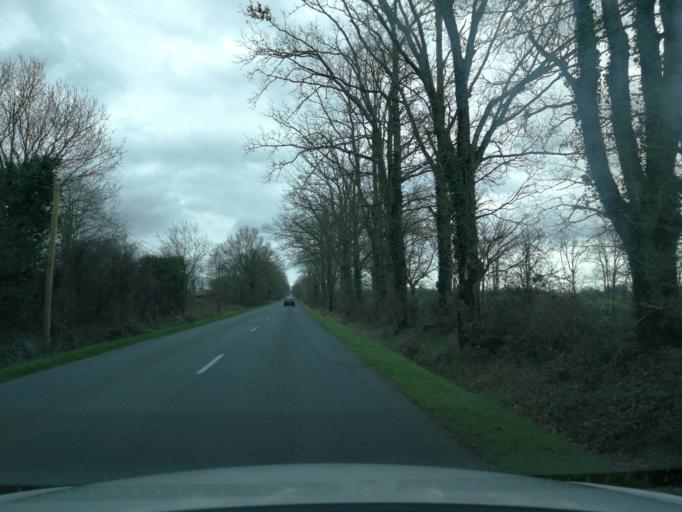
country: FR
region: Pays de la Loire
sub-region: Departement de la Loire-Atlantique
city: Montbert
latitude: 47.0165
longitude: -1.4846
